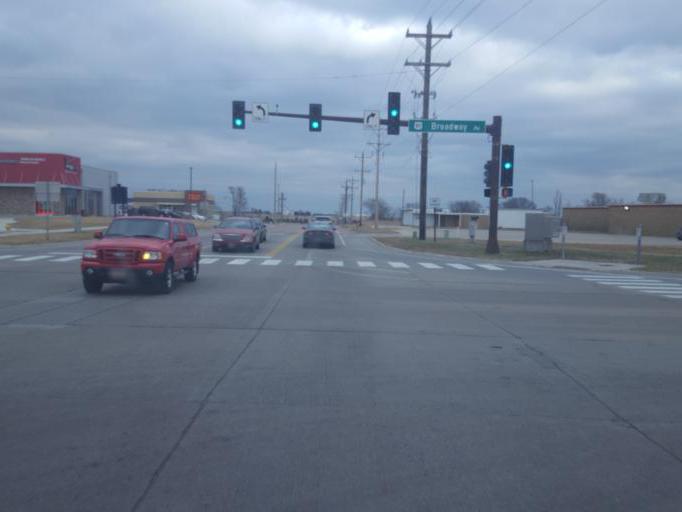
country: US
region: South Dakota
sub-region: Yankton County
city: Yankton
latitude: 42.9088
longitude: -97.3980
